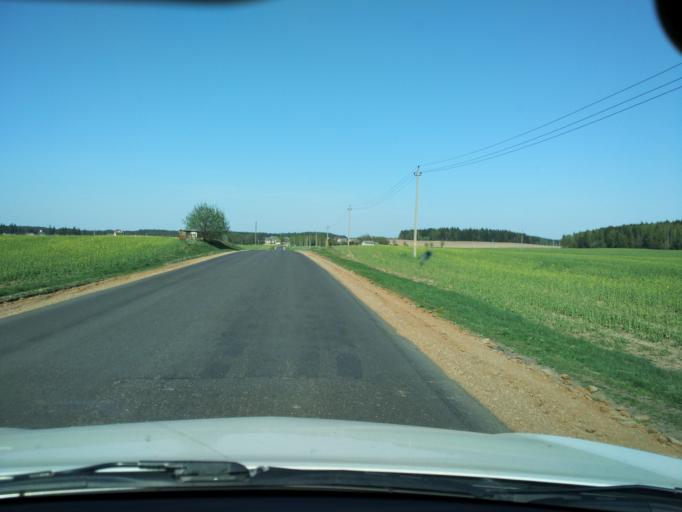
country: BY
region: Minsk
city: Lyeskawka
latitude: 54.0056
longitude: 27.7351
